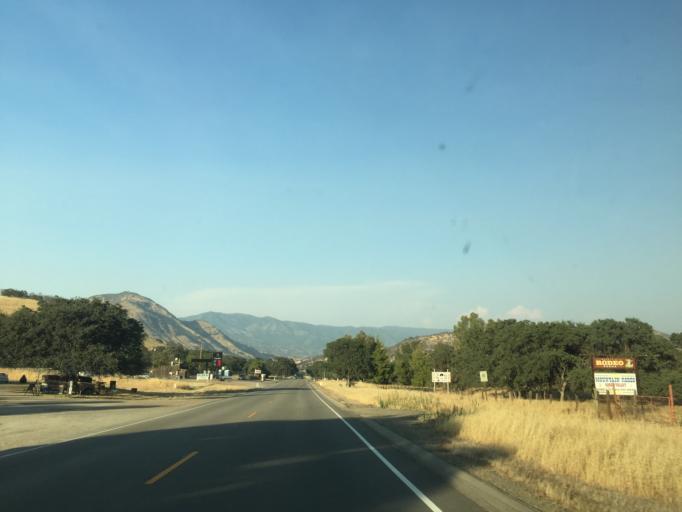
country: US
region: California
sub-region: Fresno County
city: Squaw Valley
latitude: 36.7396
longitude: -119.2499
